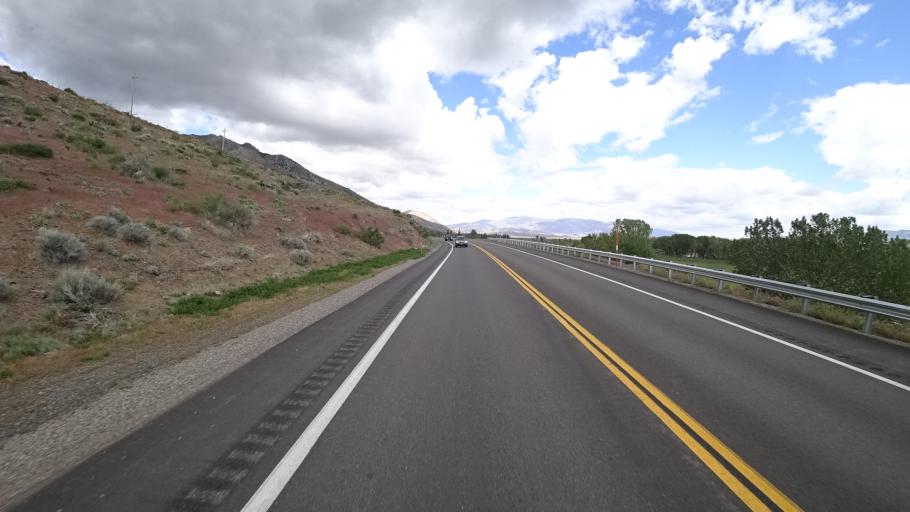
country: US
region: Nevada
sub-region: Lyon County
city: Smith Valley
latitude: 38.5831
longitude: -119.5124
